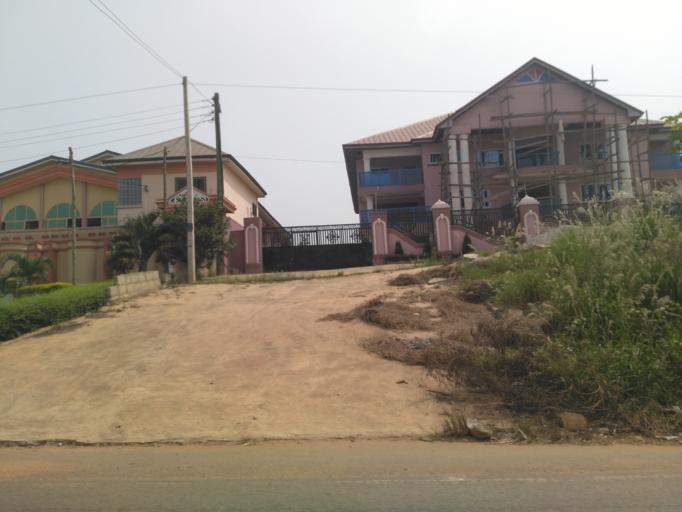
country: GH
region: Ashanti
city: Kumasi
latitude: 6.6488
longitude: -1.6435
